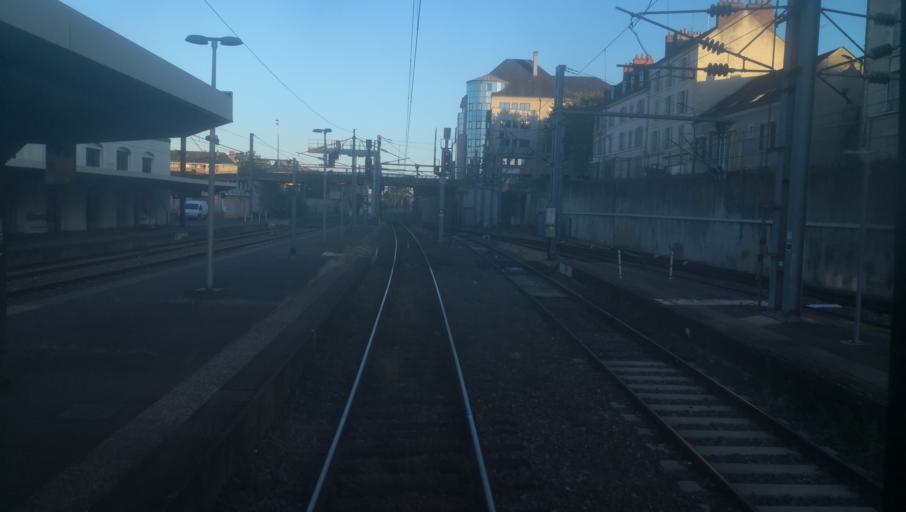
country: FR
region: Bourgogne
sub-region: Departement de la Nievre
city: Nevers
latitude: 46.9868
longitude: 3.1505
